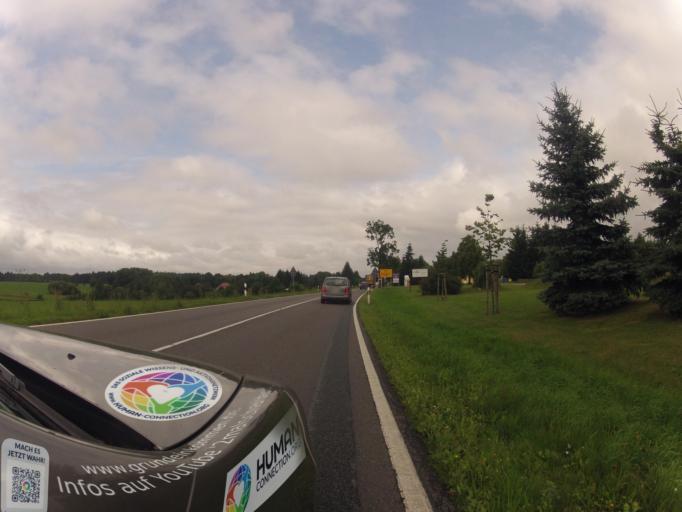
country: DE
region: Mecklenburg-Vorpommern
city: Anklam
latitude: 53.9044
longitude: 13.7469
